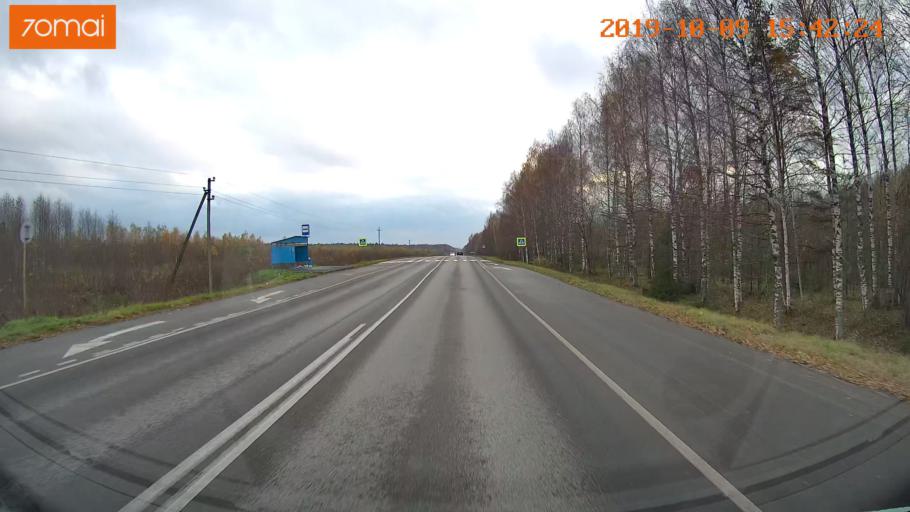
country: RU
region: Kostroma
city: Oktyabr'skiy
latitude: 57.8688
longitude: 41.1076
